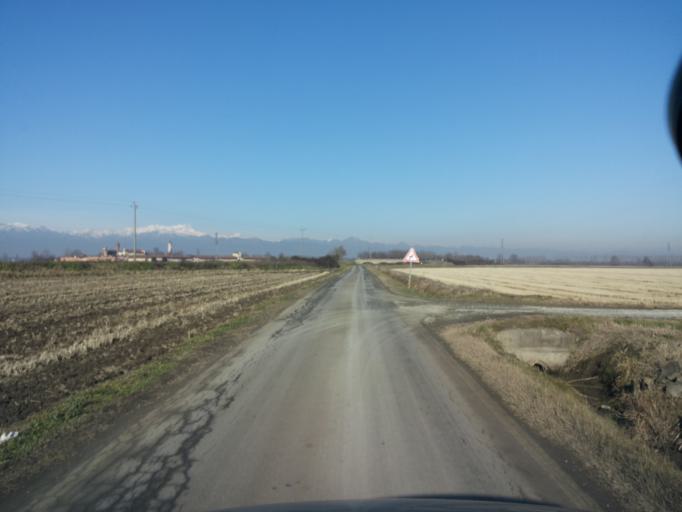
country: IT
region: Piedmont
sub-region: Provincia di Vercelli
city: San Germano Vercellese
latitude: 45.3868
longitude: 8.2442
